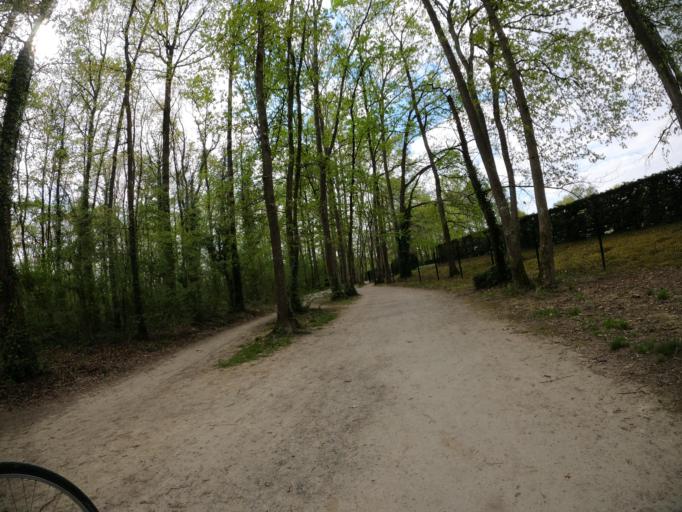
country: FR
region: Aquitaine
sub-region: Departement des Pyrenees-Atlantiques
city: Lons
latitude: 43.3236
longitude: -0.3946
